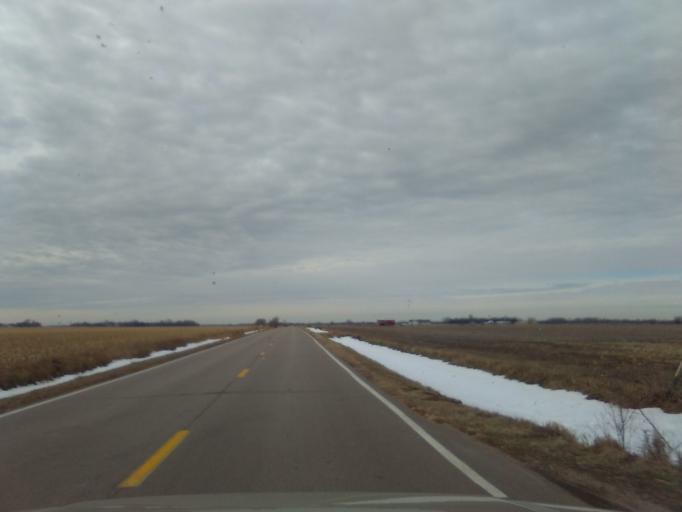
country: US
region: Nebraska
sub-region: Hall County
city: Wood River
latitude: 40.7710
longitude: -98.4357
